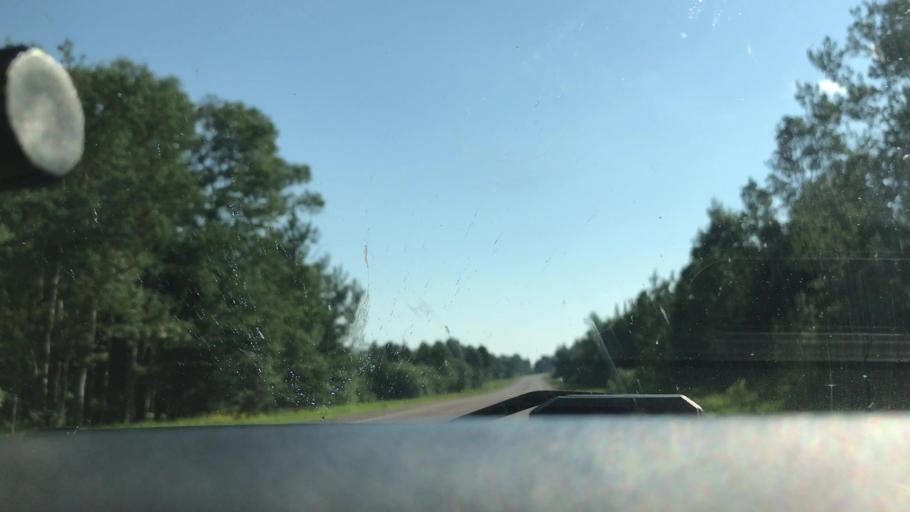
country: US
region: Minnesota
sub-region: Cook County
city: Grand Marais
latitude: 47.8040
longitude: -90.0948
